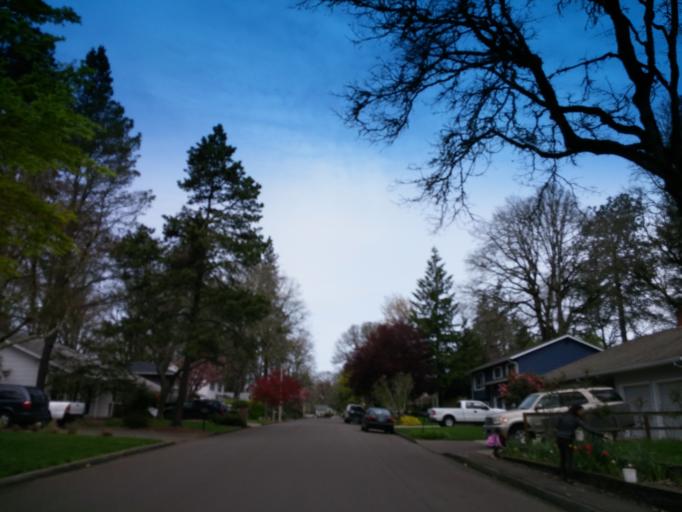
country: US
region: Oregon
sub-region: Washington County
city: Cedar Mill
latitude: 45.5314
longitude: -122.8176
